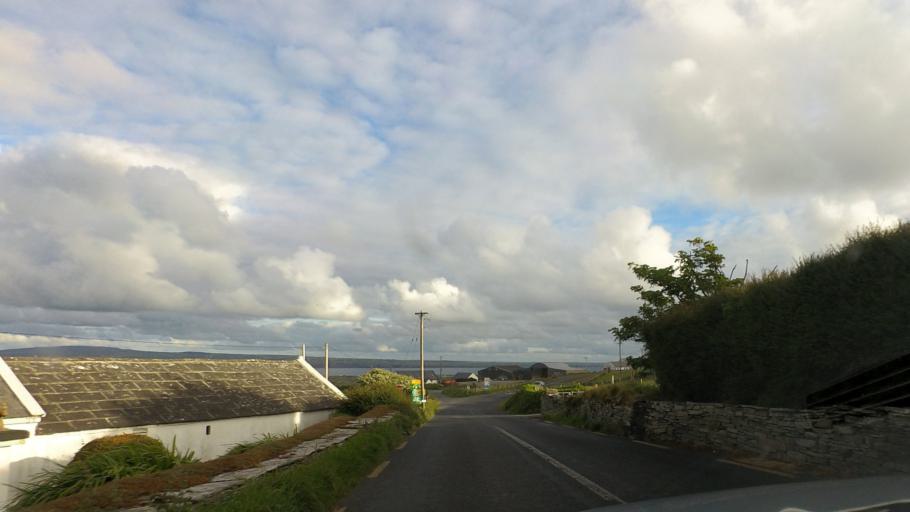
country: IE
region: Munster
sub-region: An Clar
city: Kilrush
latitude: 52.9548
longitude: -9.4207
